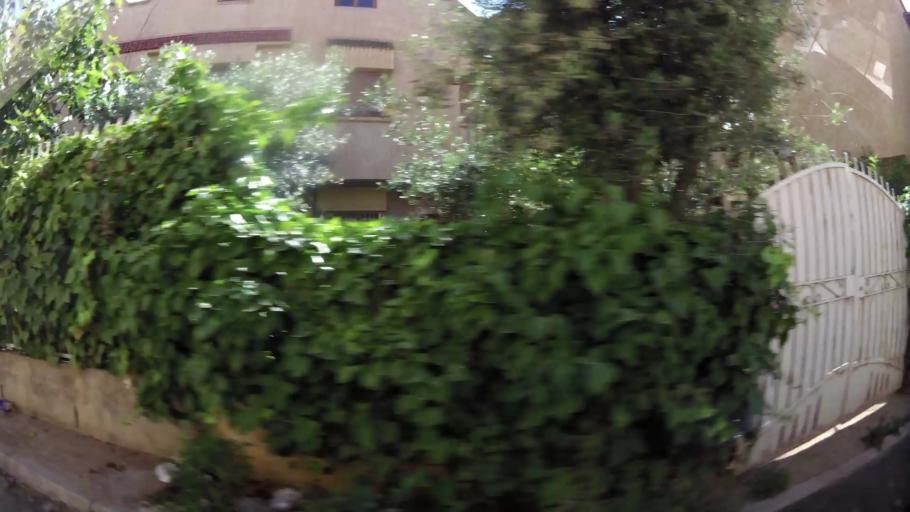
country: MA
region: Oriental
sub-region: Oujda-Angad
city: Oujda
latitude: 34.6938
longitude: -1.8704
